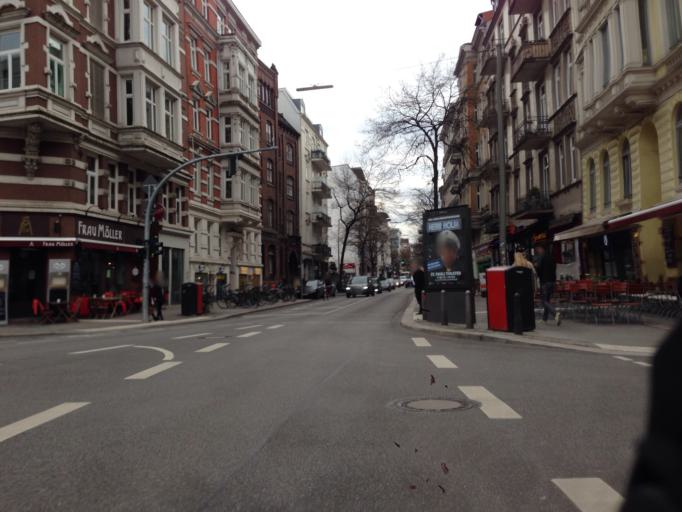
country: DE
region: Hamburg
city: St. Georg
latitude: 53.5590
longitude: 10.0134
